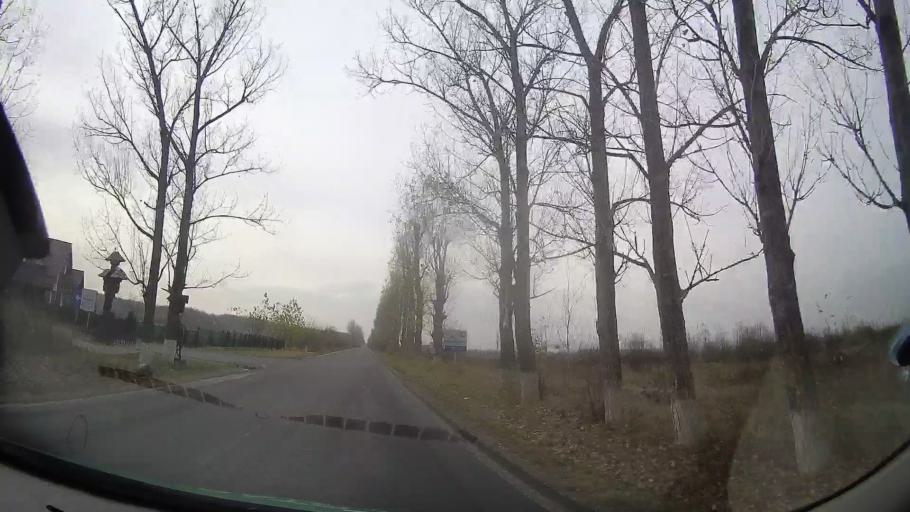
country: RO
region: Prahova
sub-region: Comuna Balta Doamnei
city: Balta Doamnei
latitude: 44.7439
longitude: 26.1504
